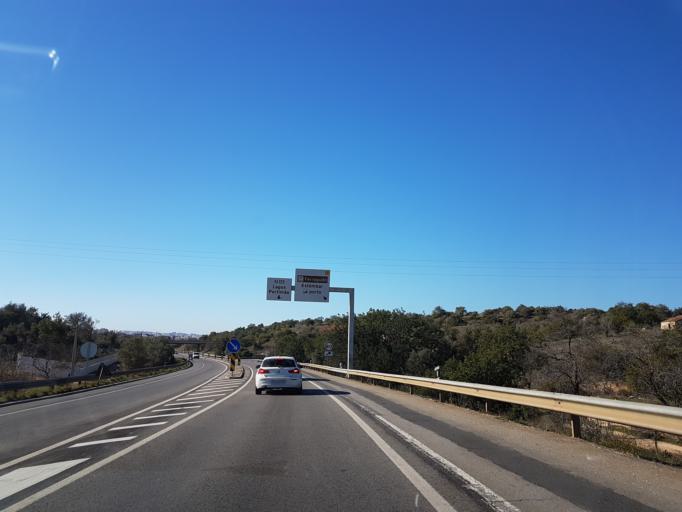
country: PT
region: Faro
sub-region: Lagoa
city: Estombar
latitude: 37.1531
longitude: -8.4922
